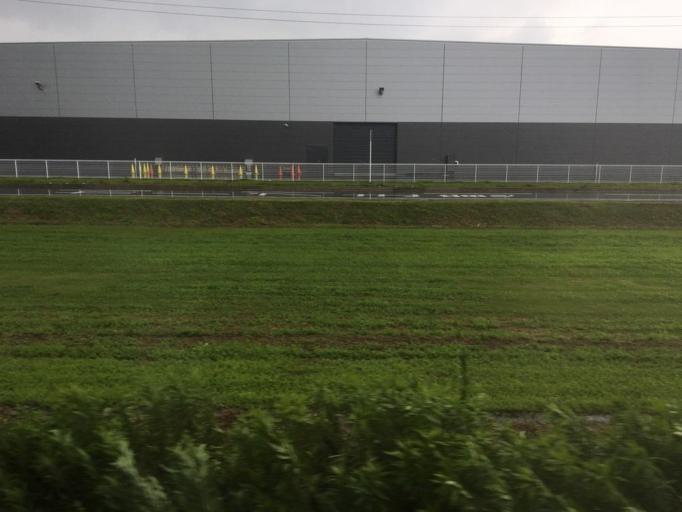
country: JP
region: Tochigi
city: Ashikaga
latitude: 36.2887
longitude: 139.4757
